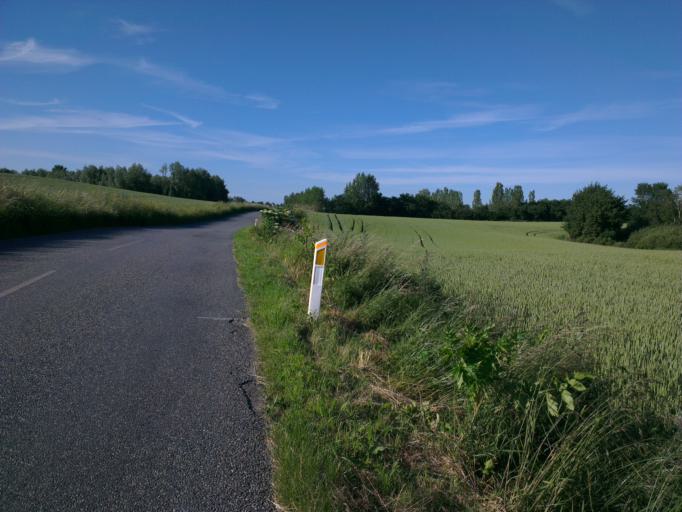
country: DK
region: Capital Region
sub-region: Frederikssund Kommune
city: Skibby
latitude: 55.7435
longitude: 12.0334
